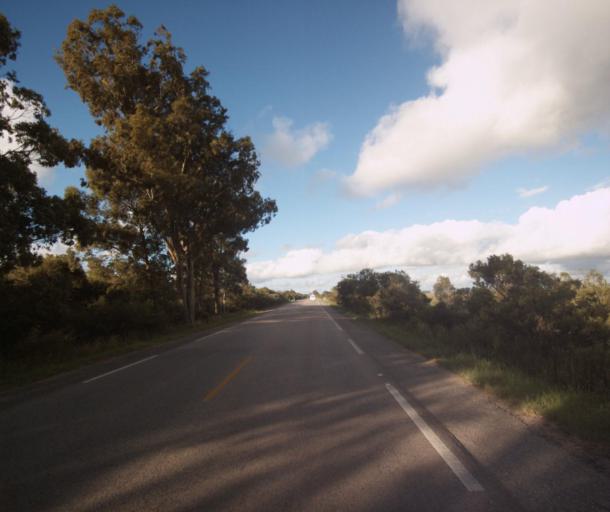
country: BR
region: Rio Grande do Sul
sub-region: Rio Grande
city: Rio Grande
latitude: -32.1850
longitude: -52.4276
